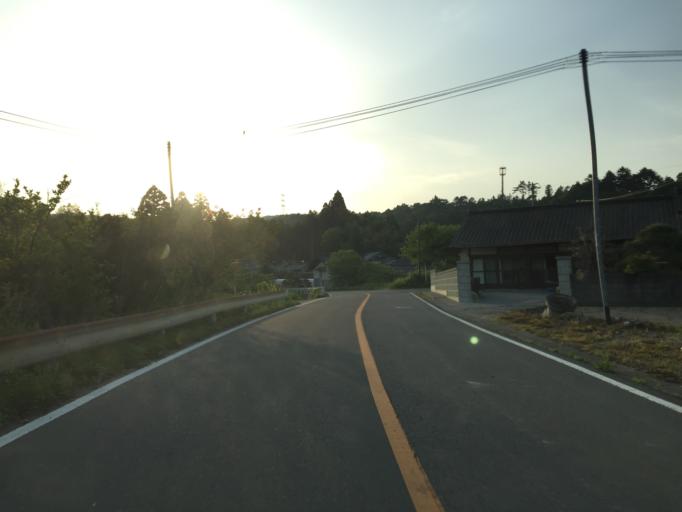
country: JP
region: Fukushima
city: Iwaki
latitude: 37.2200
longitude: 140.9714
